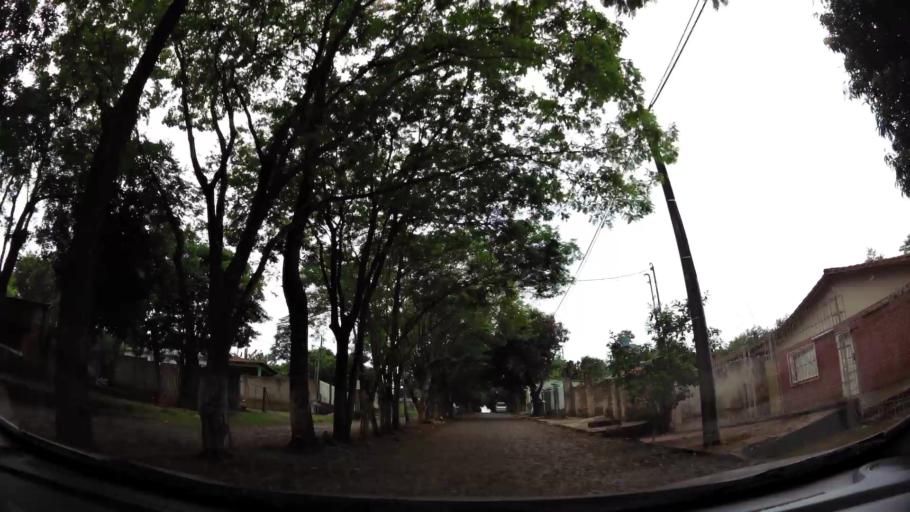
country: BR
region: Parana
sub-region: Foz Do Iguacu
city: Foz do Iguacu
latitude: -25.5444
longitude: -54.6034
